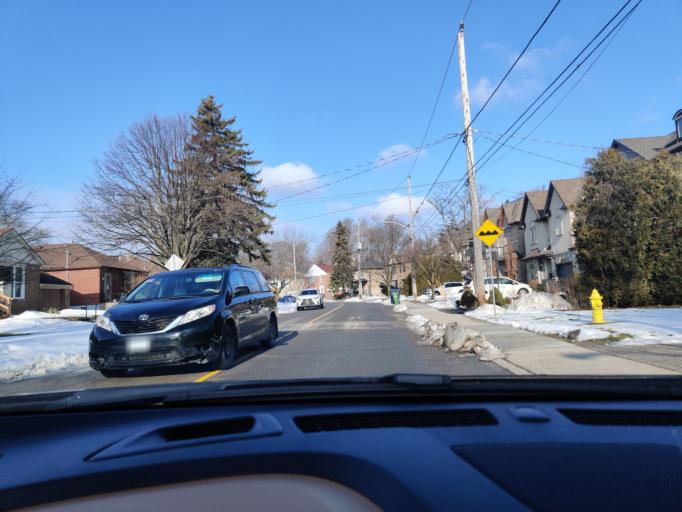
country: CA
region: Ontario
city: Toronto
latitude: 43.7251
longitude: -79.4335
